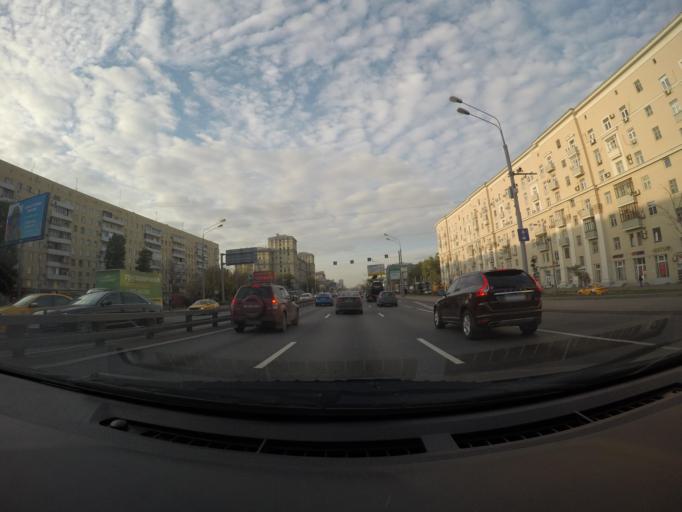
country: RU
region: Moskovskaya
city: Koptevo
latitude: 55.8166
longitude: 37.5000
